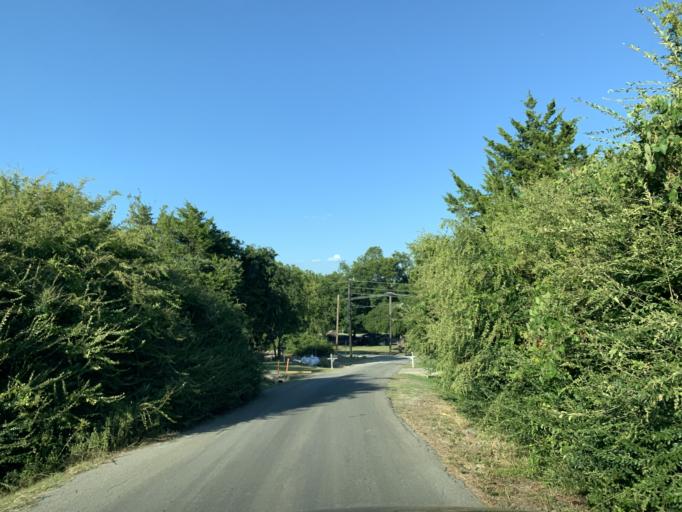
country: US
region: Texas
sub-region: Dallas County
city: Hutchins
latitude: 32.6727
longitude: -96.7766
